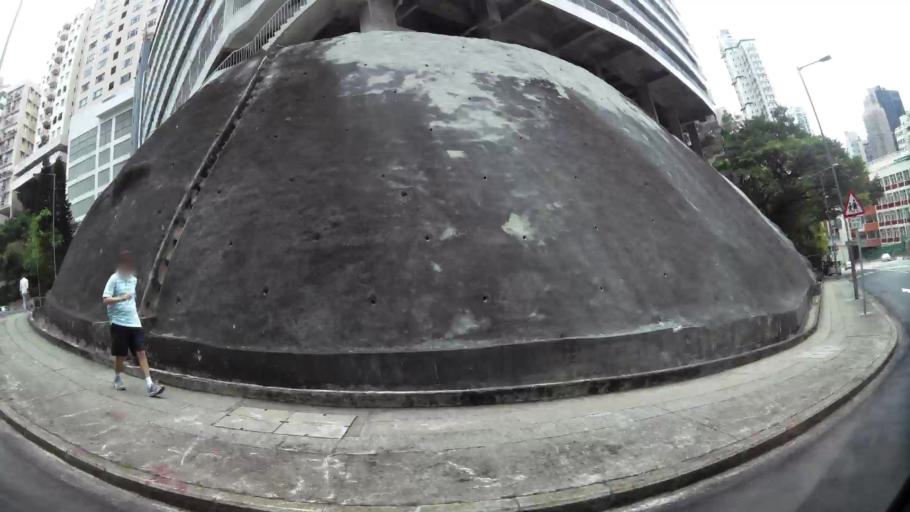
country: HK
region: Wanchai
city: Wan Chai
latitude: 22.2860
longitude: 114.1941
